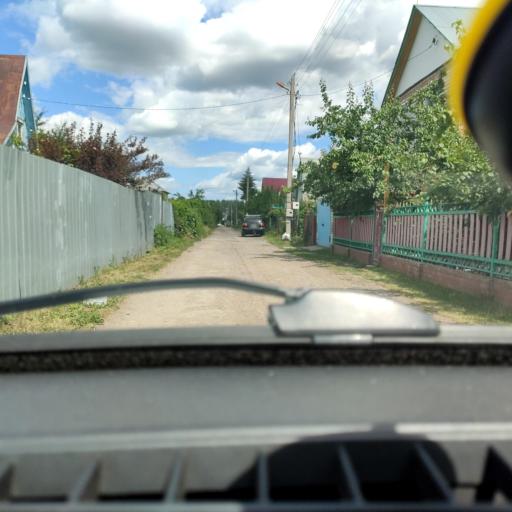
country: RU
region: Samara
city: Podstepki
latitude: 53.6025
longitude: 49.2257
